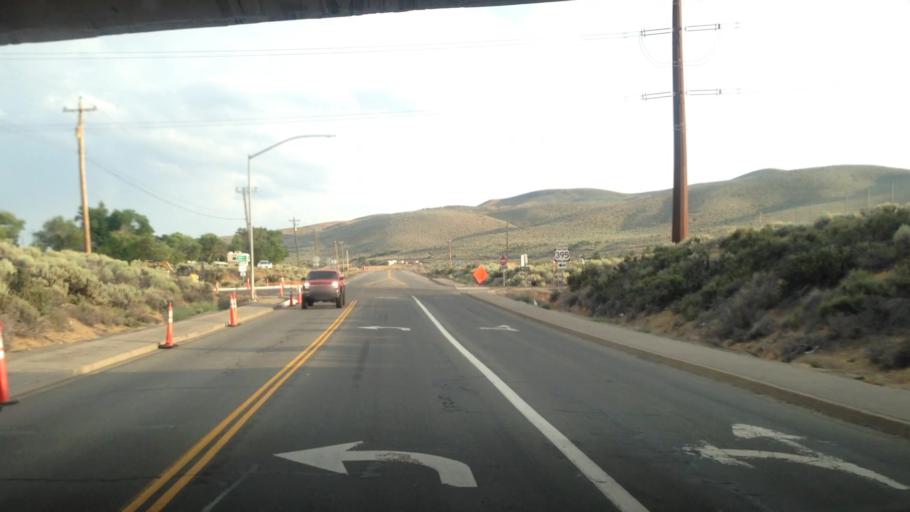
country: US
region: Nevada
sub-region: Washoe County
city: Lemmon Valley
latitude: 39.6189
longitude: -119.8822
